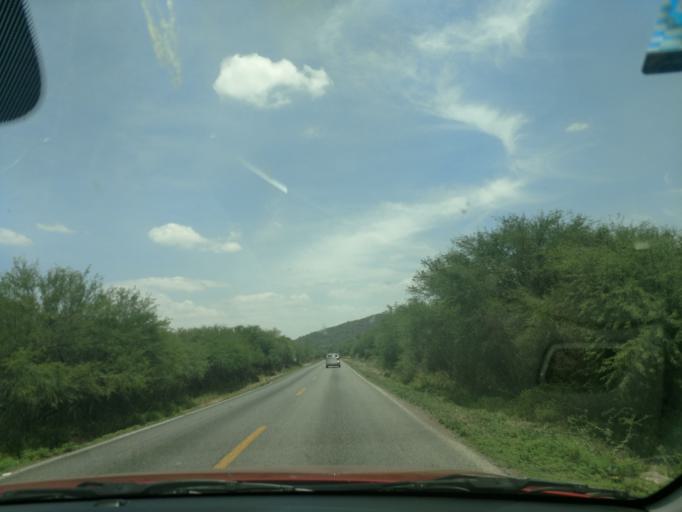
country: MX
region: San Luis Potosi
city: Ciudad Fernandez
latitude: 21.9995
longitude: -100.1414
